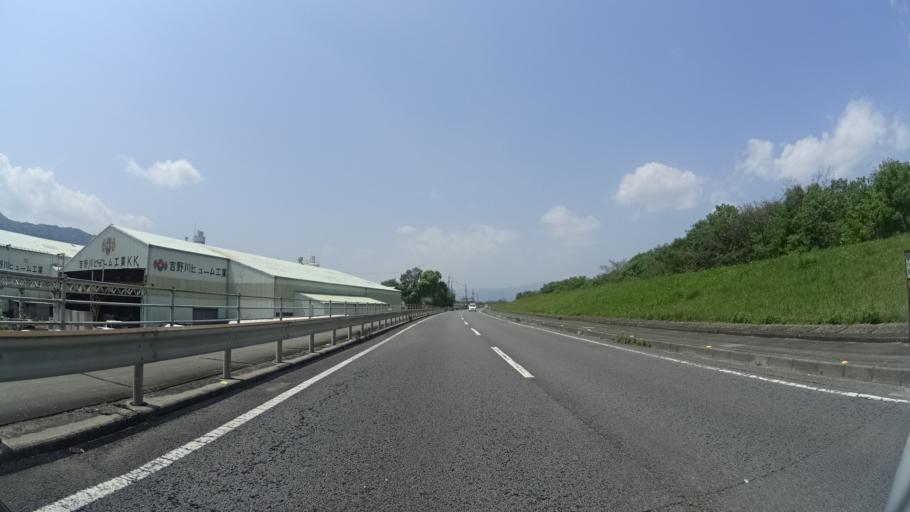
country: JP
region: Tokushima
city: Kamojimacho-jogejima
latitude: 34.0613
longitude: 134.2952
